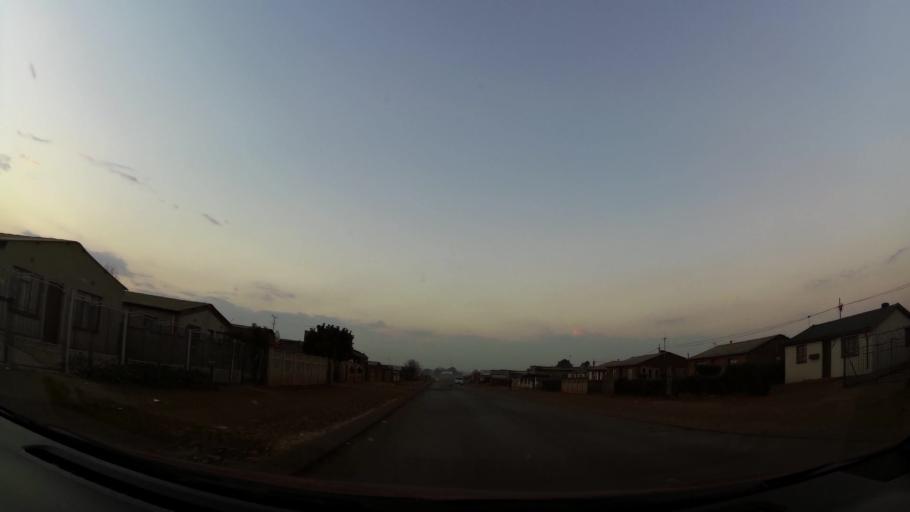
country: ZA
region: Gauteng
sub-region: City of Johannesburg Metropolitan Municipality
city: Orange Farm
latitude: -26.5562
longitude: 27.8625
